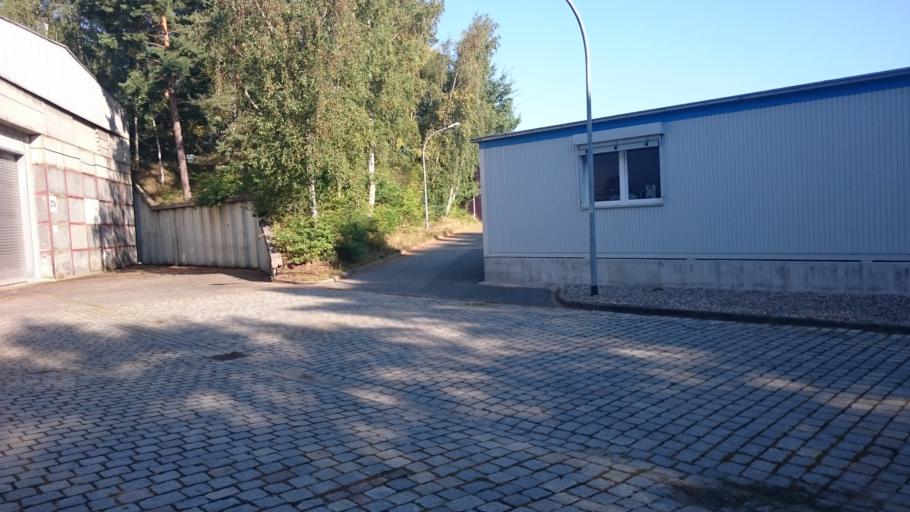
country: DE
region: Hamburg
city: Eidelstedt
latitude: 53.5774
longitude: 9.8805
